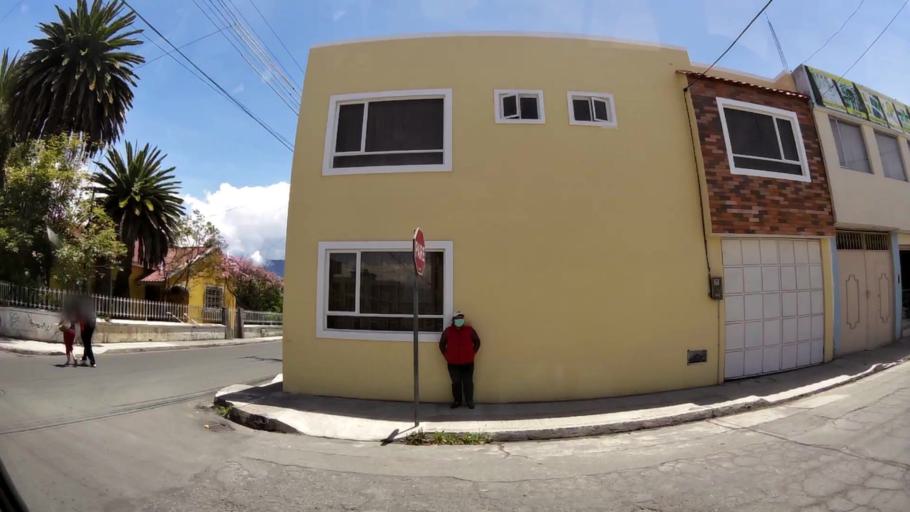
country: EC
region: Chimborazo
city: Riobamba
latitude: -1.6740
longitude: -78.6420
